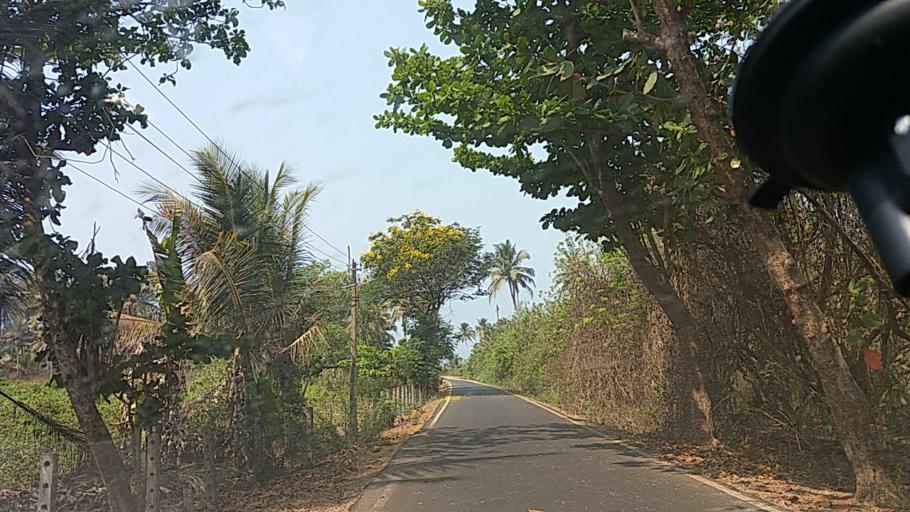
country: IN
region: Goa
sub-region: South Goa
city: Sancoale
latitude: 15.3358
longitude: 73.8956
